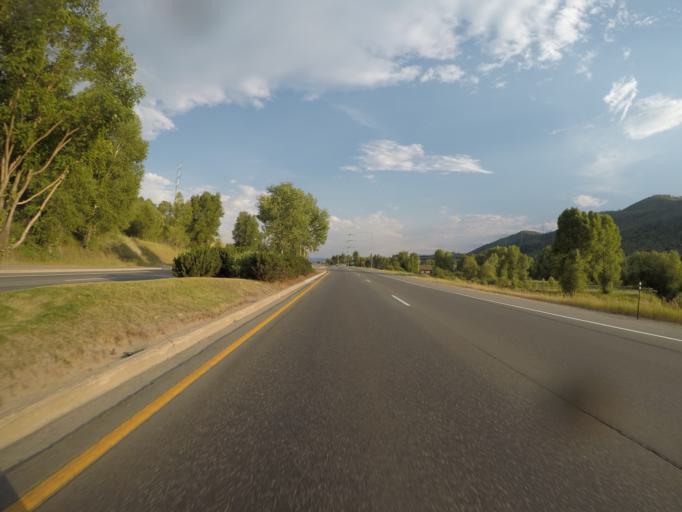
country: US
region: Colorado
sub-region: Routt County
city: Steamboat Springs
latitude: 40.4709
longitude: -106.8264
